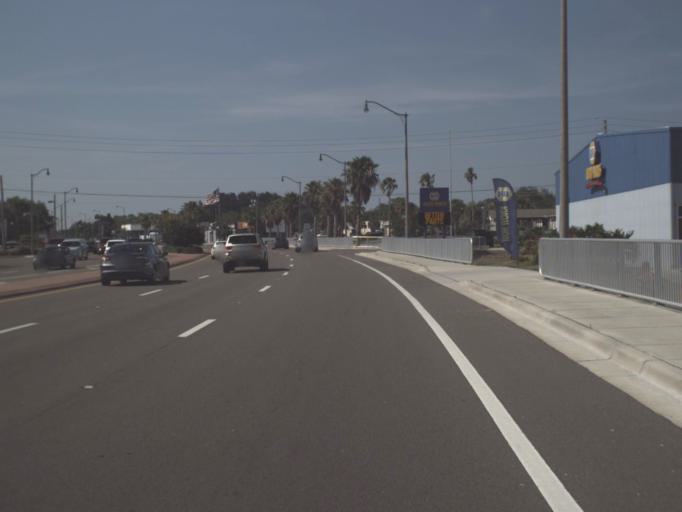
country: US
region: Florida
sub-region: Brevard County
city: Rockledge
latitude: 28.3580
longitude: -80.7324
